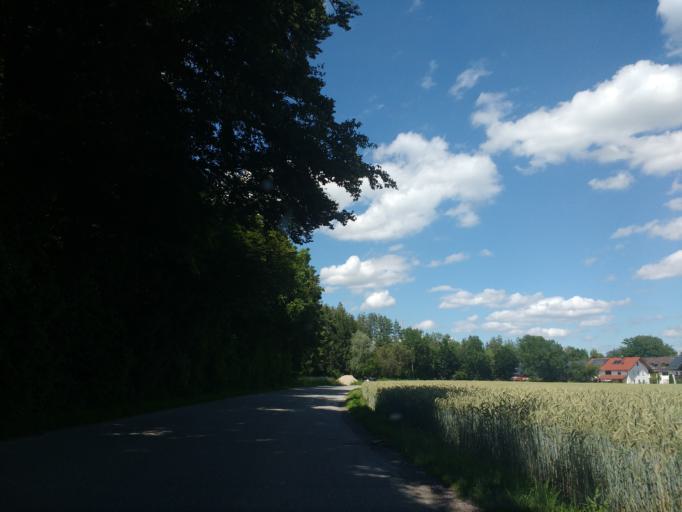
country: DE
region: Bavaria
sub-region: Upper Bavaria
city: Mehring
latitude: 48.2056
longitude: 12.7614
